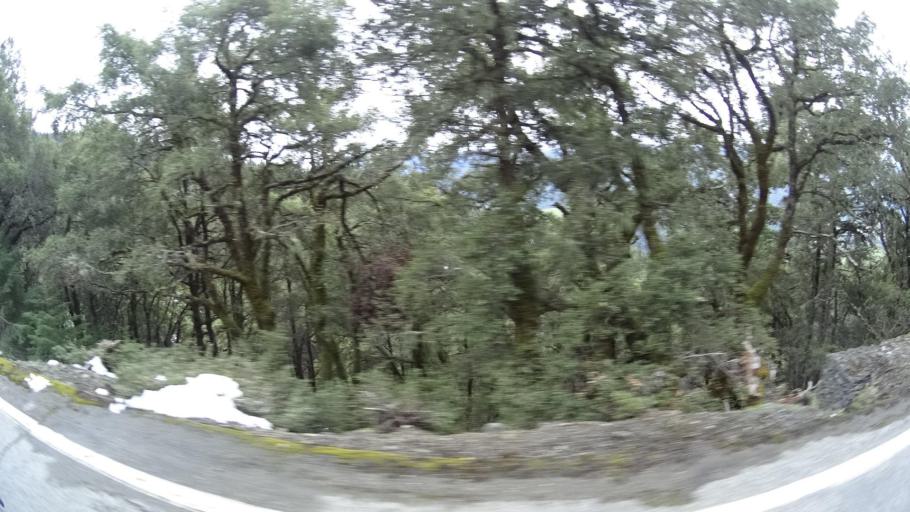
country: US
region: California
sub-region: Humboldt County
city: Willow Creek
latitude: 40.8798
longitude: -123.7612
